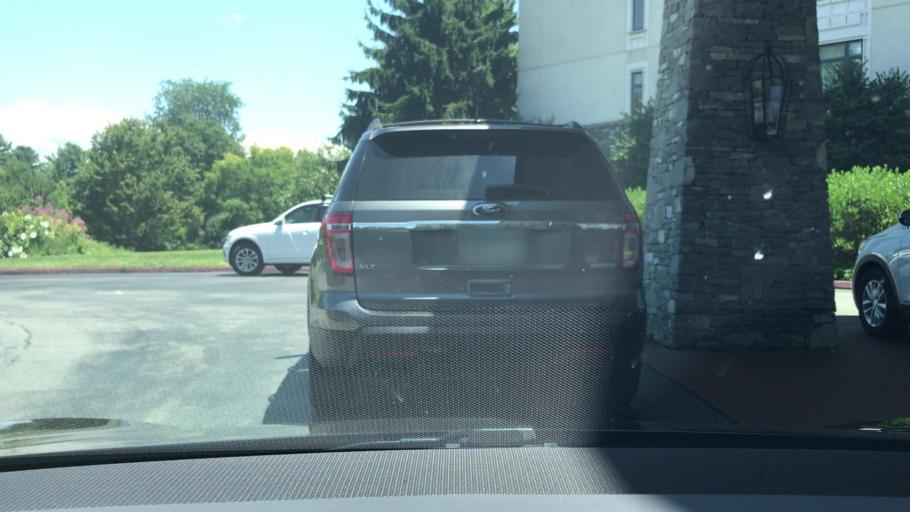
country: US
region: North Carolina
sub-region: Buncombe County
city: Asheville
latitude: 35.5581
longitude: -82.5807
